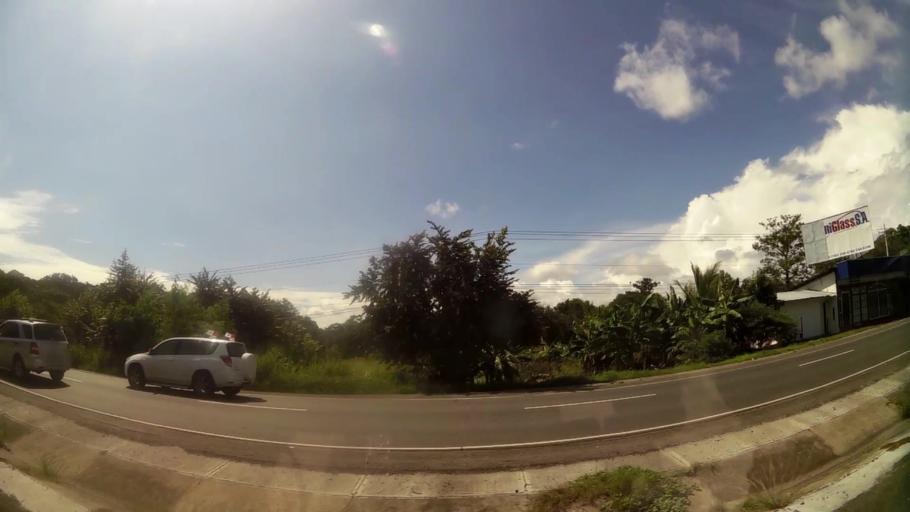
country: PA
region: Panama
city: Chame
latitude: 8.5738
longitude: -79.8844
